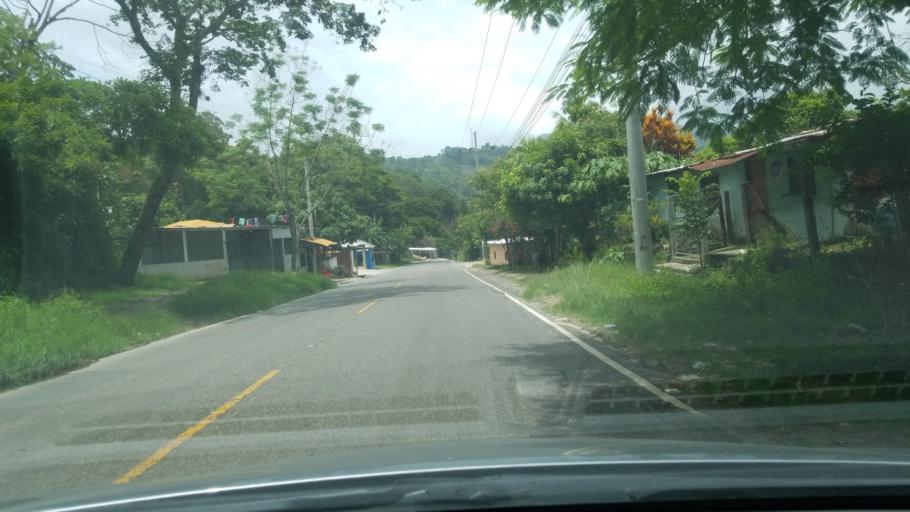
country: HN
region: Copan
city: Ojos de Agua
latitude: 14.6785
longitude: -88.8186
